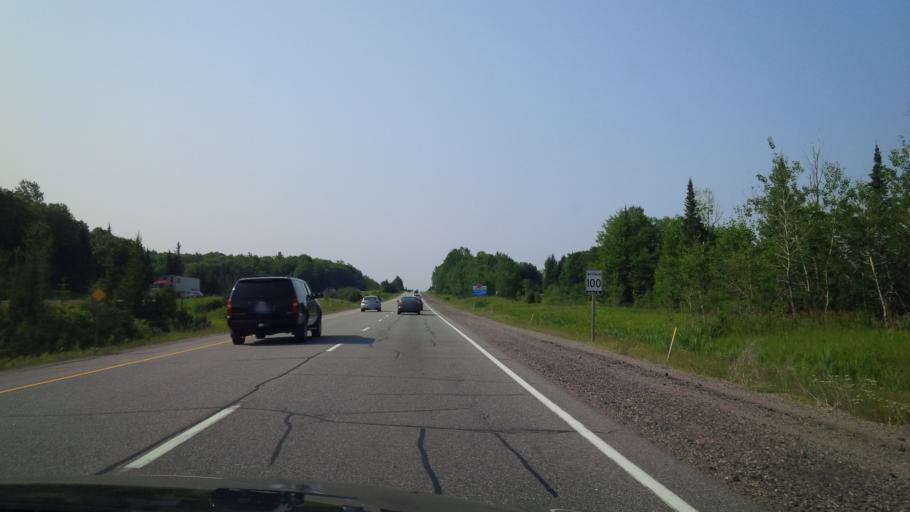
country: CA
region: Ontario
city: Bracebridge
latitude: 45.1942
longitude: -79.3137
